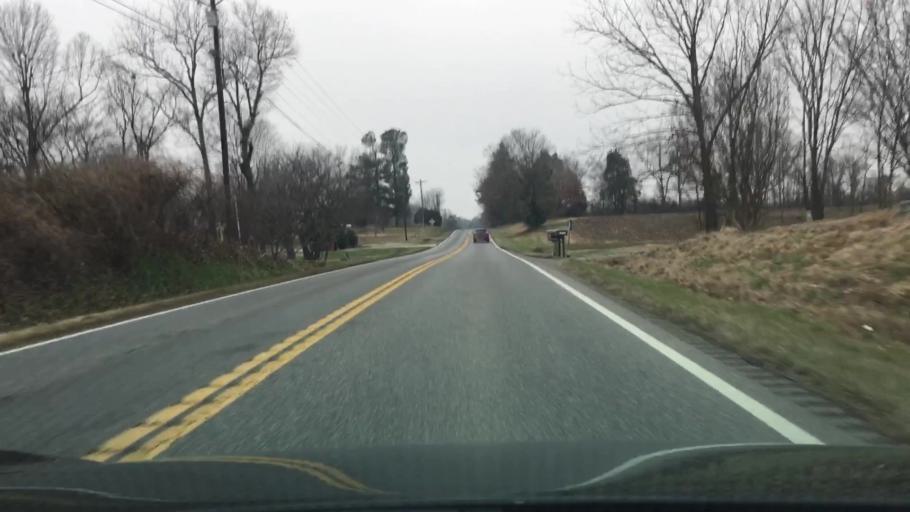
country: US
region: Kentucky
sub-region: Livingston County
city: Ledbetter
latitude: 36.9662
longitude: -88.4402
